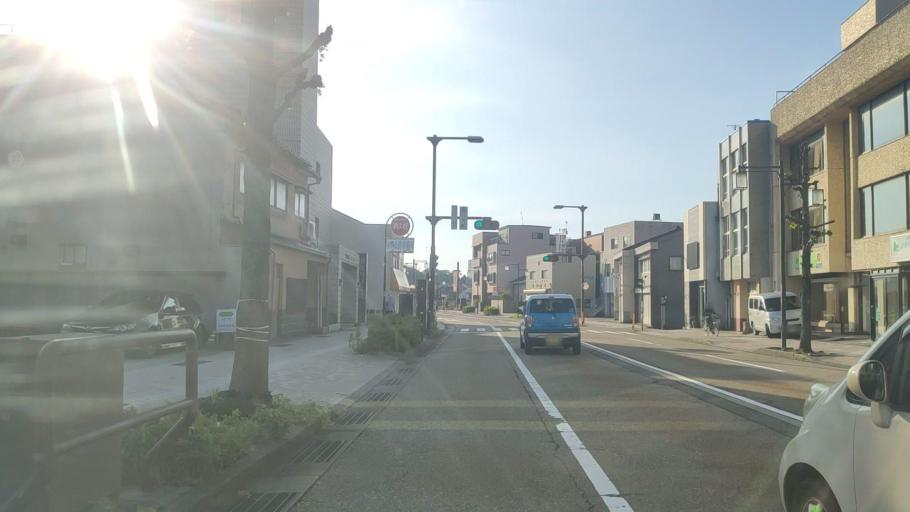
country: JP
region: Ishikawa
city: Kanazawa-shi
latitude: 36.5646
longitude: 136.6664
